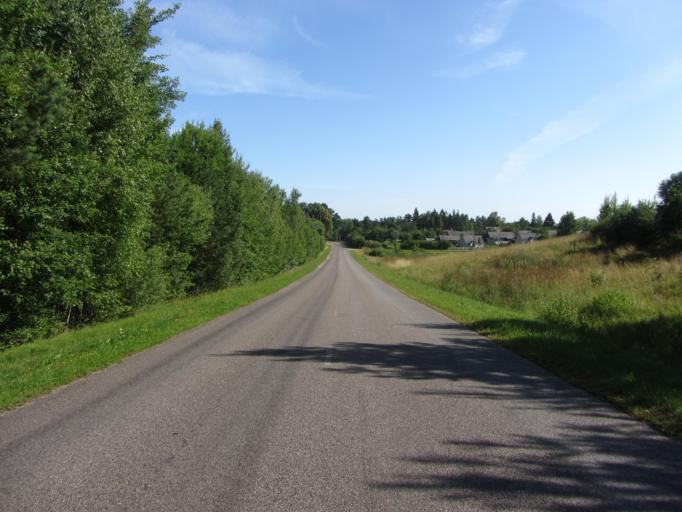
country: LT
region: Vilnius County
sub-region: Vilniaus Rajonas
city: Vievis
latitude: 54.8086
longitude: 24.8252
